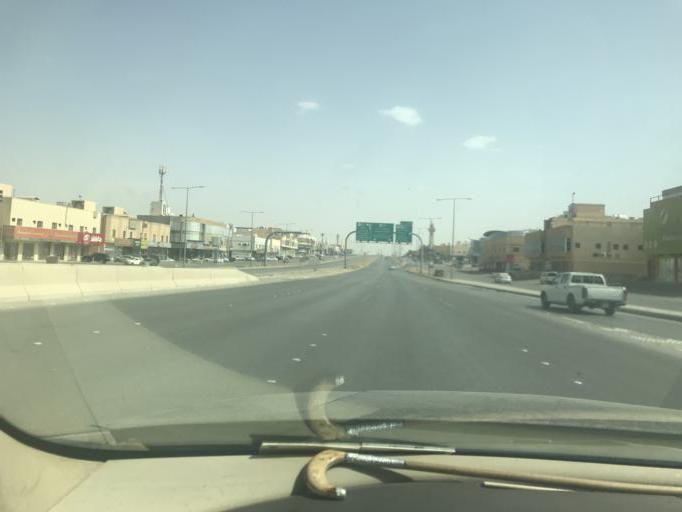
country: SA
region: Ar Riyad
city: Riyadh
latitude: 24.7749
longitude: 46.7093
